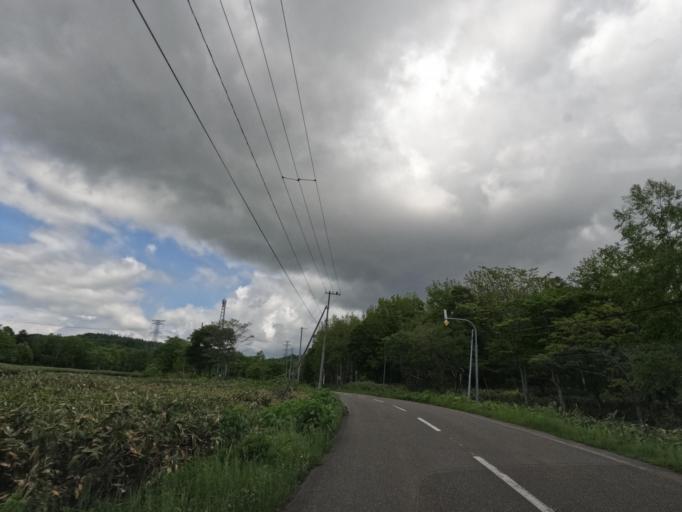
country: JP
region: Hokkaido
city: Tobetsu
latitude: 43.4625
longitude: 141.5978
